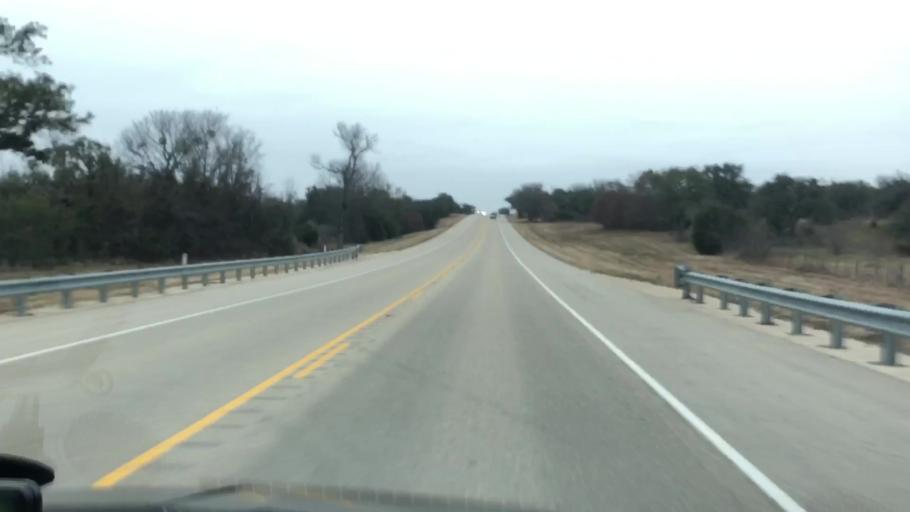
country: US
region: Texas
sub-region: Hamilton County
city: Hamilton
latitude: 31.5567
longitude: -98.1595
